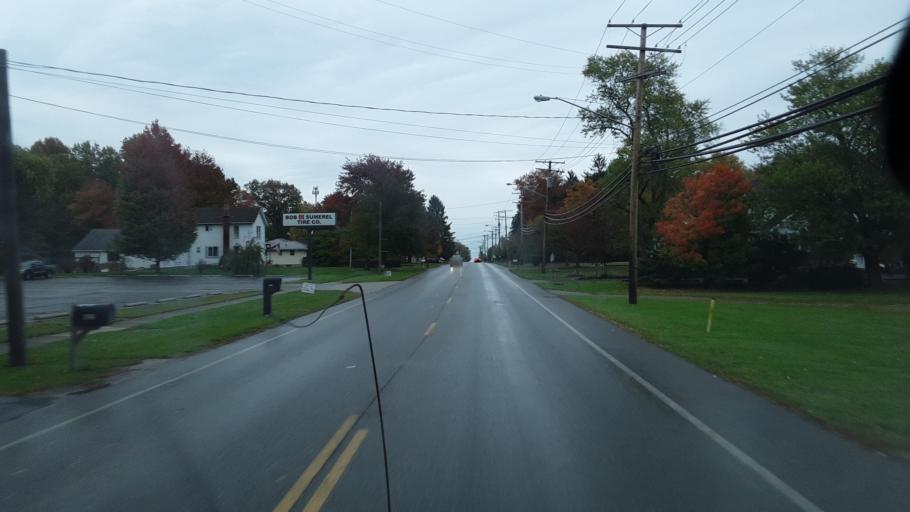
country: US
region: Ohio
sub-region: Ashtabula County
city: Orwell
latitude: 41.5351
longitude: -80.8526
